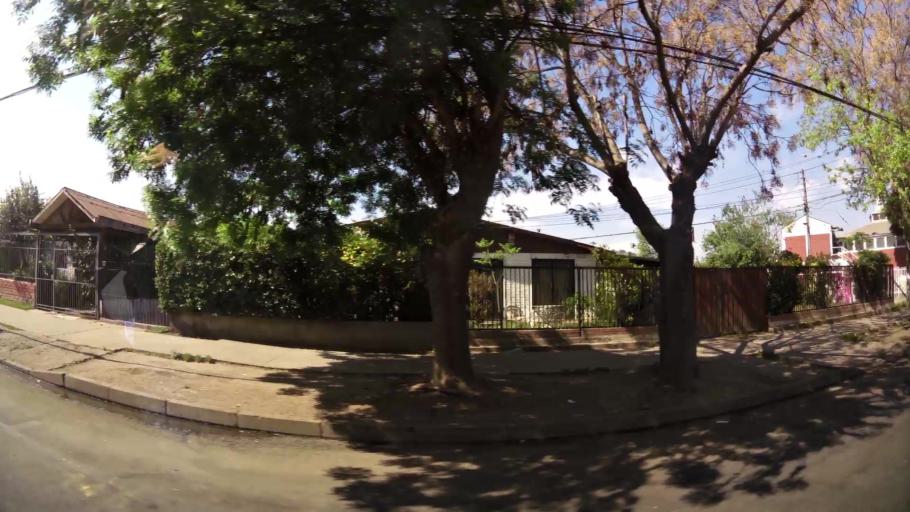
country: CL
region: Santiago Metropolitan
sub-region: Provincia de Santiago
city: Lo Prado
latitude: -33.4739
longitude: -70.7305
